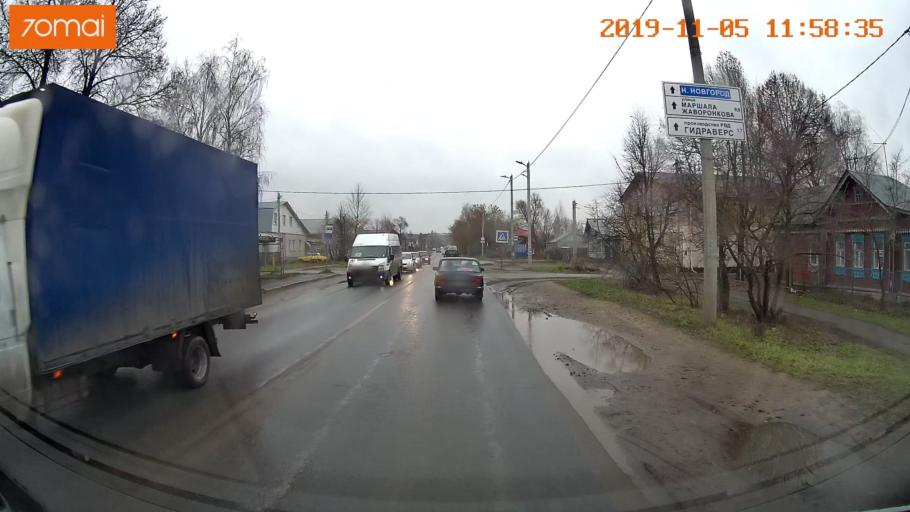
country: RU
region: Ivanovo
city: Kokhma
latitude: 56.9808
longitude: 41.0406
